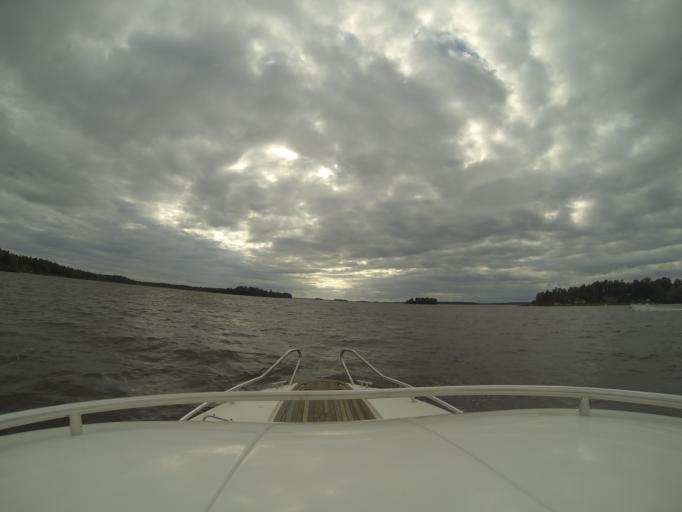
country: SE
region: Soedermanland
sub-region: Eskilstuna Kommun
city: Kvicksund
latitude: 59.4528
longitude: 16.3065
